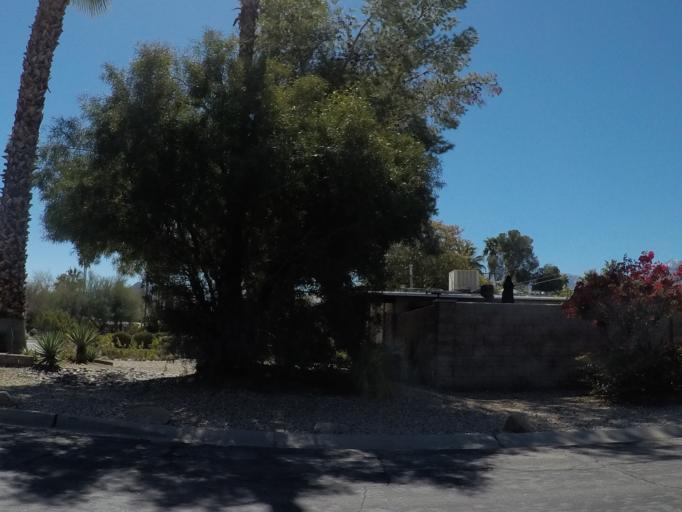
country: US
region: California
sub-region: Riverside County
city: Palm Springs
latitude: 33.8268
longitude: -116.5209
